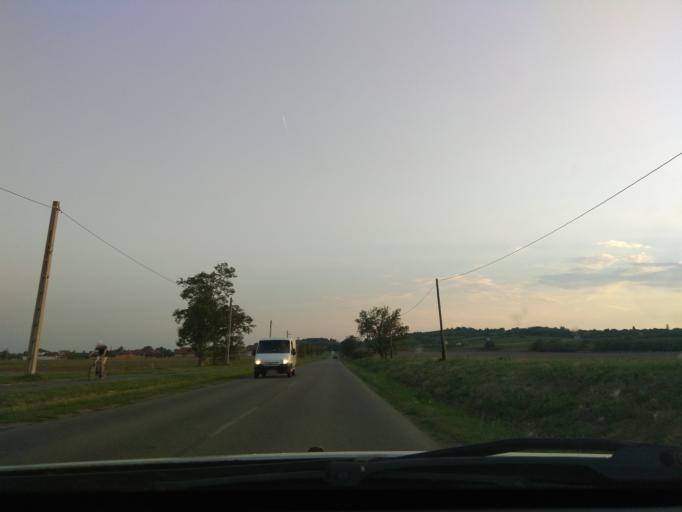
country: HU
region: Borsod-Abauj-Zemplen
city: Szerencs
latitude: 48.1809
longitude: 21.2058
